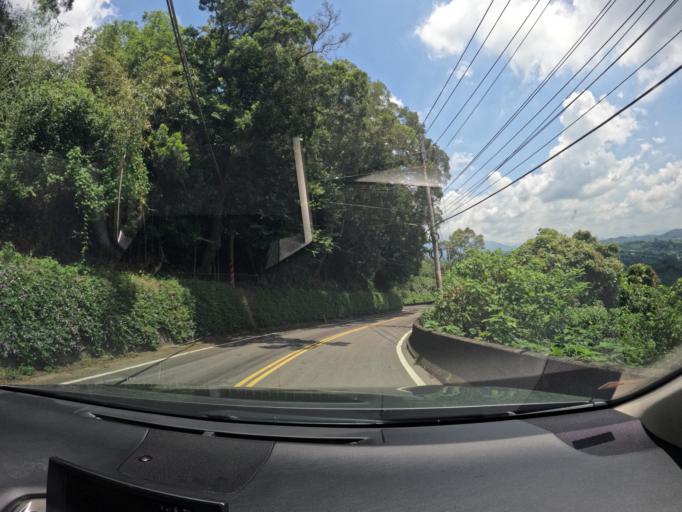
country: TW
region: Taiwan
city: Fengyuan
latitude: 24.3735
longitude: 120.8380
